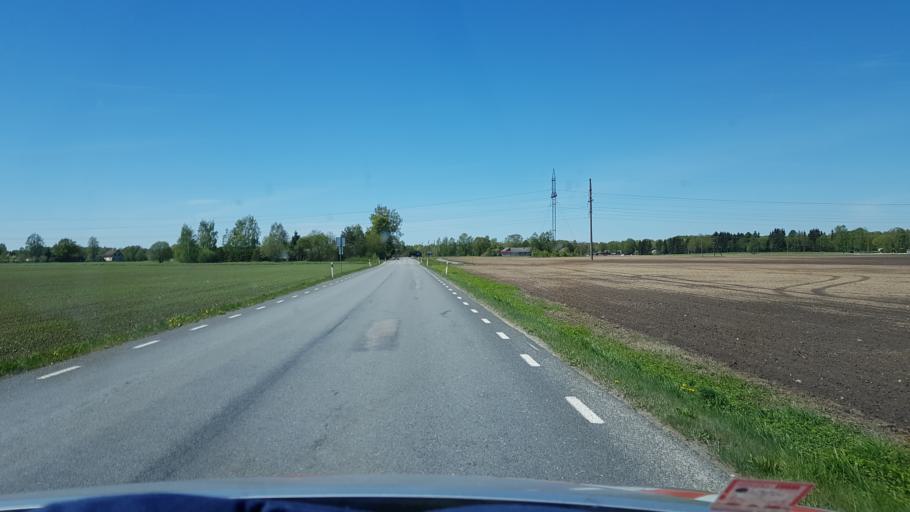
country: EE
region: Tartu
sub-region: UElenurme vald
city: Ulenurme
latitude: 58.3176
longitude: 26.6314
